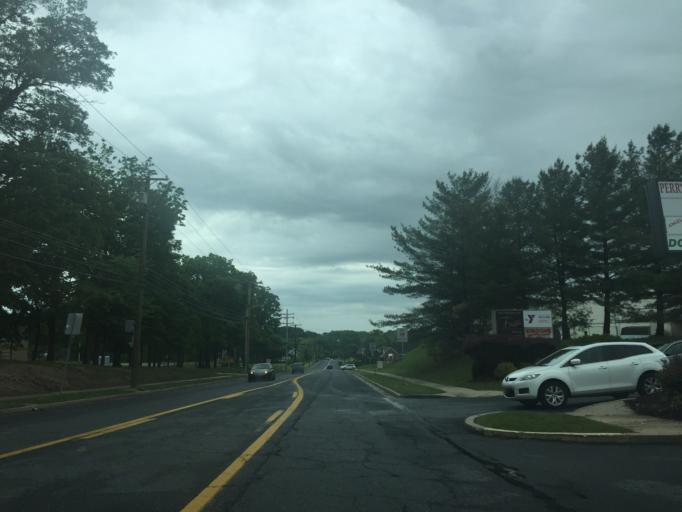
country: US
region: Maryland
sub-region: Baltimore County
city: Perry Hall
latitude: 39.3975
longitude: -76.4759
